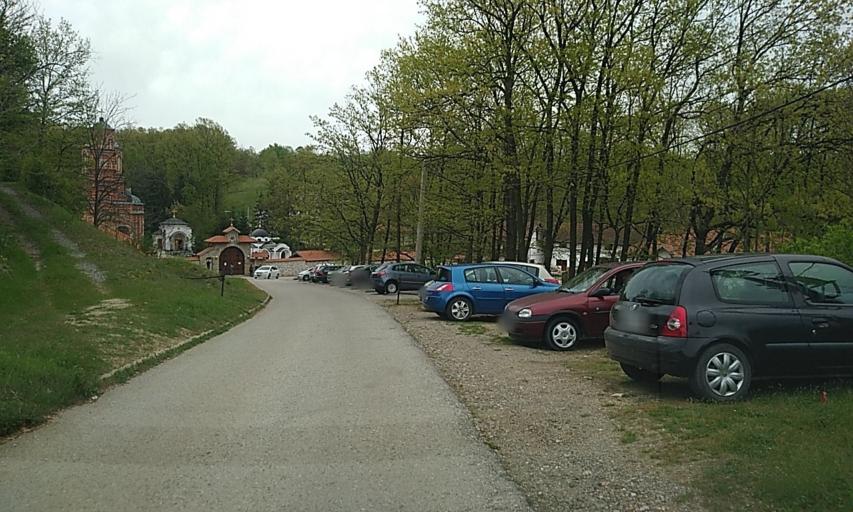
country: RS
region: Central Serbia
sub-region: Nisavski Okrug
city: Razanj
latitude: 43.5721
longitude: 21.5280
